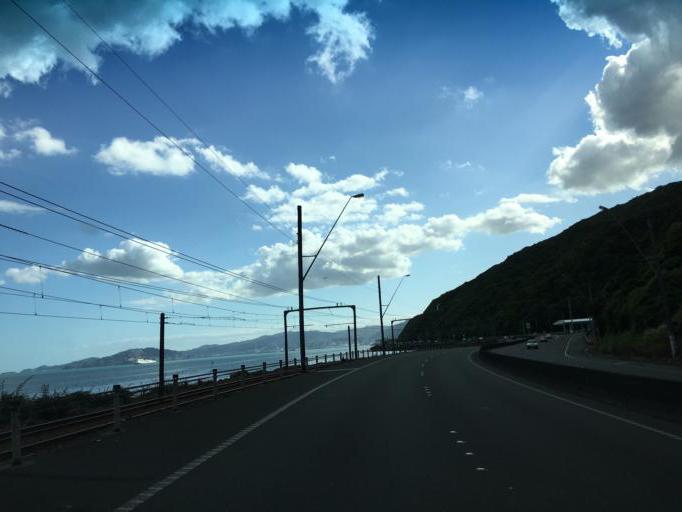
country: NZ
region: Wellington
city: Petone
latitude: -41.2311
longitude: 174.8409
